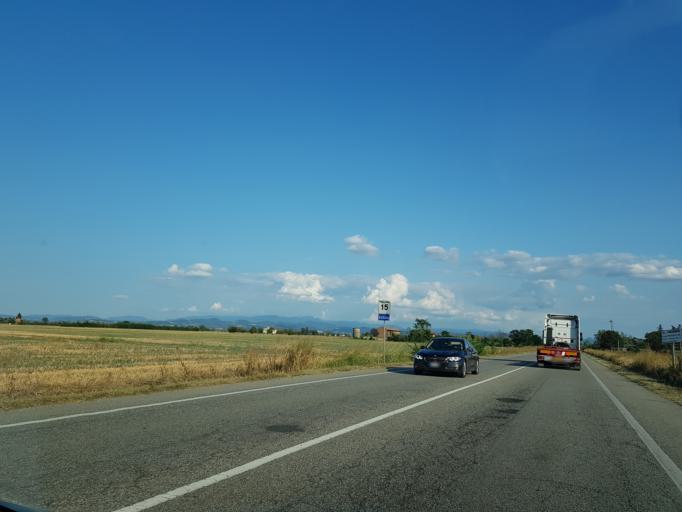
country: IT
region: Piedmont
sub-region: Provincia di Alessandria
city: Mandrogne
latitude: 44.8255
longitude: 8.7470
